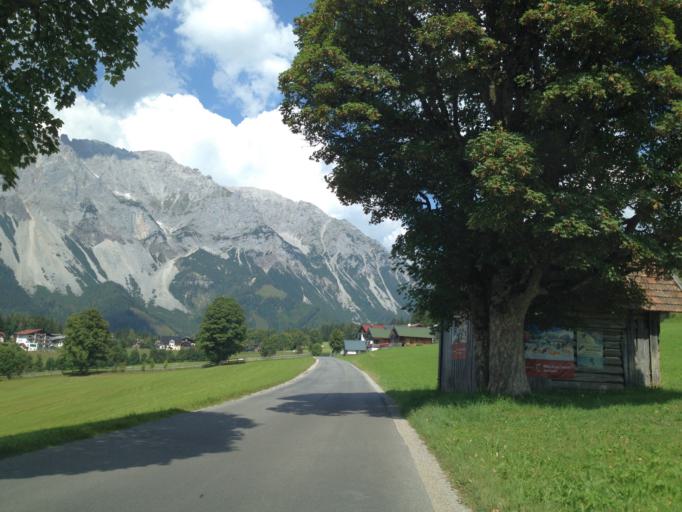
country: AT
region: Styria
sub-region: Politischer Bezirk Liezen
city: Schladming
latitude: 47.4130
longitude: 13.6354
